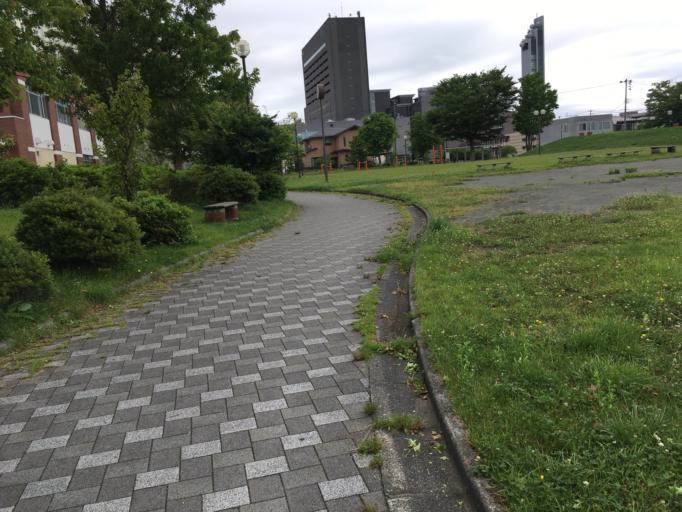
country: JP
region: Akita
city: Akita
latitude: 39.7132
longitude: 140.1305
